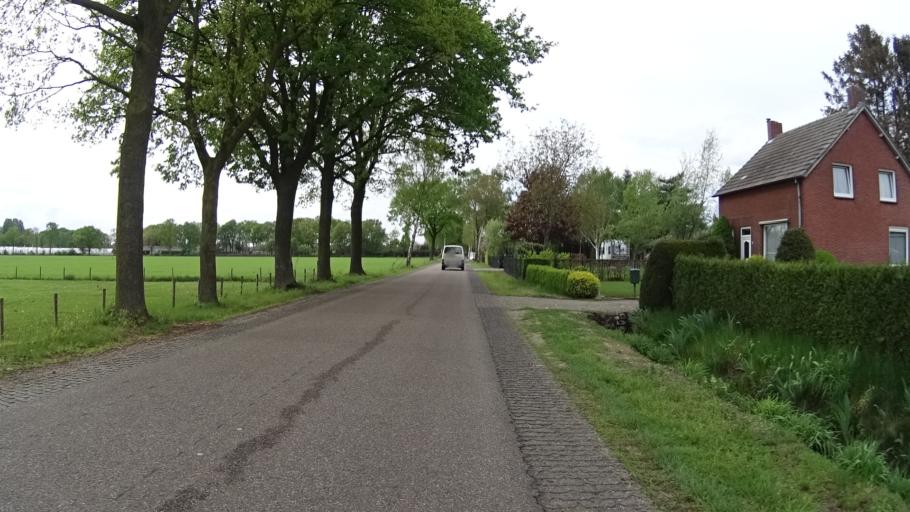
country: NL
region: North Brabant
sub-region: Gemeente Veghel
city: Mariaheide
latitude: 51.6244
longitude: 5.5920
